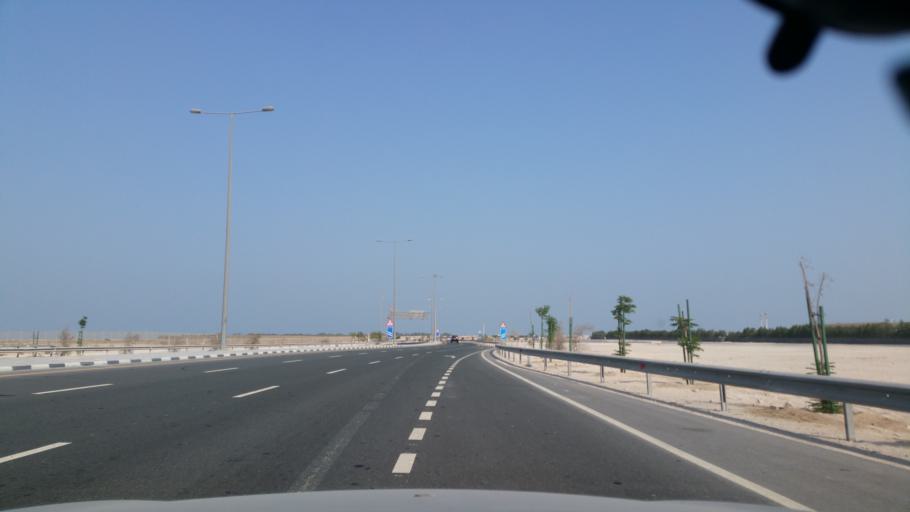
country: QA
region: Baladiyat Umm Salal
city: Umm Salal `Ali
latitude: 25.4567
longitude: 51.4852
